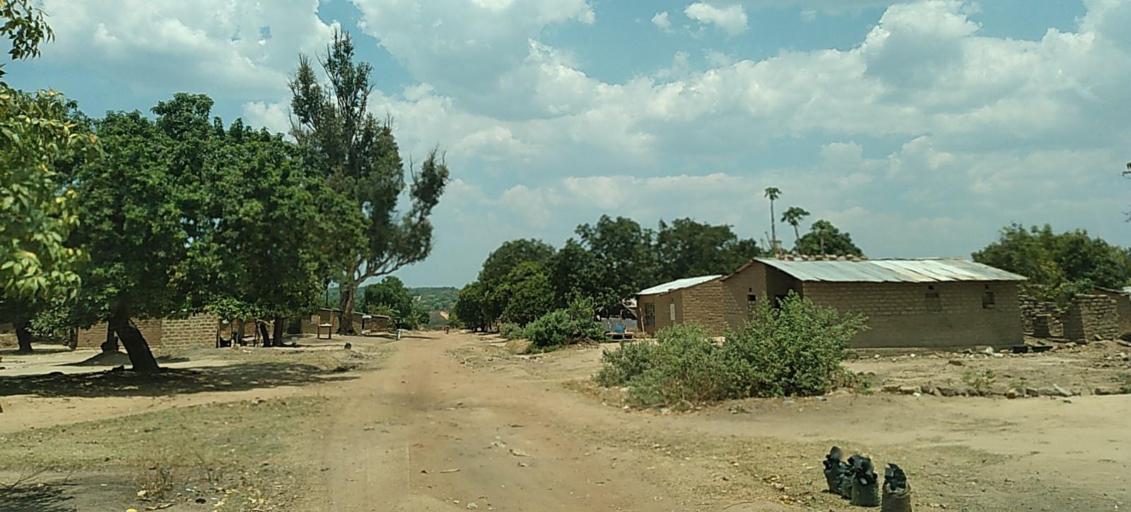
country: ZM
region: Copperbelt
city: Luanshya
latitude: -13.3687
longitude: 28.4119
